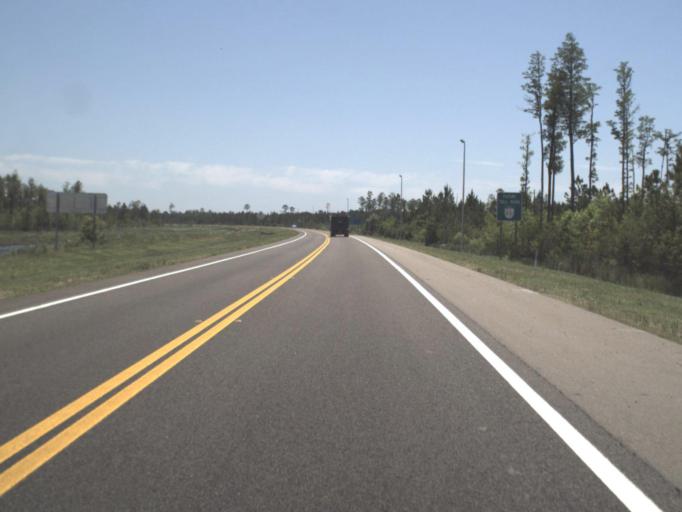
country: US
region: Florida
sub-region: Duval County
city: Baldwin
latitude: 30.2736
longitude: -81.8751
